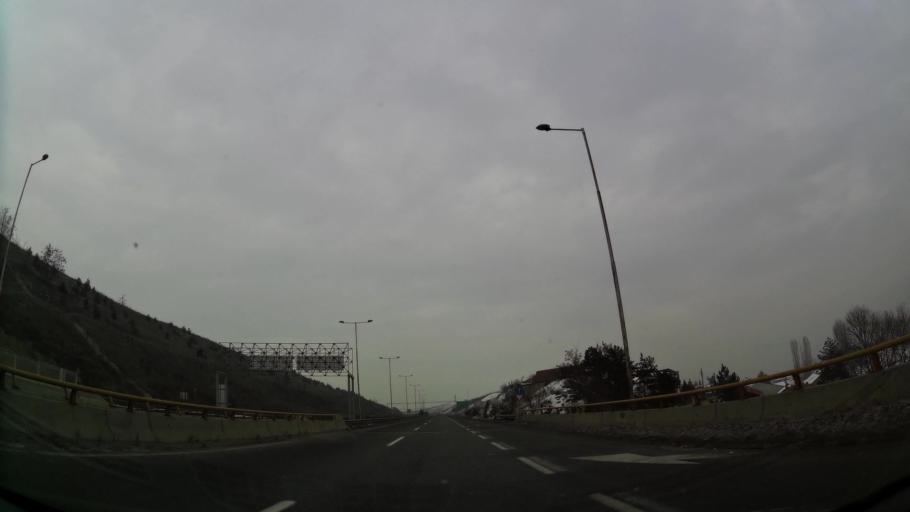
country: MK
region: Saraj
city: Saraj
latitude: 42.0098
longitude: 21.3249
